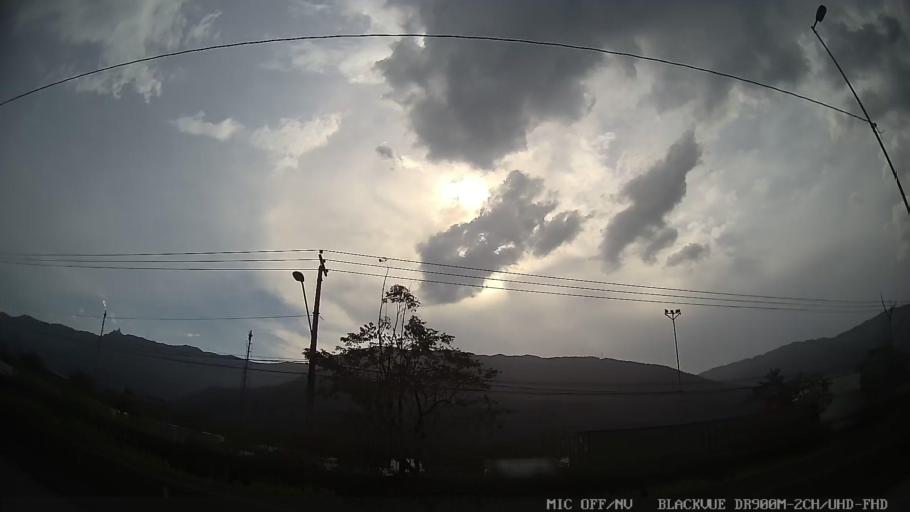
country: BR
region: Sao Paulo
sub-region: Cubatao
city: Cubatao
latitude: -23.8653
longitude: -46.4171
